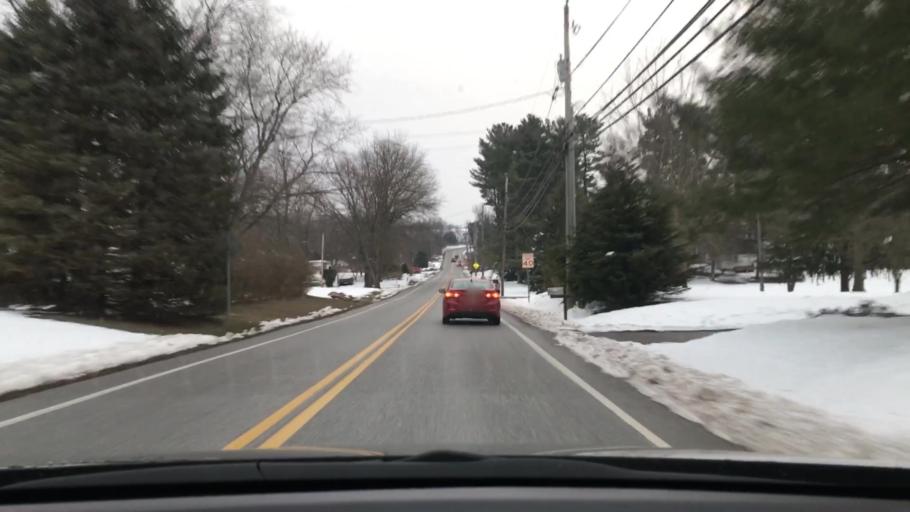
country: US
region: Pennsylvania
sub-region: York County
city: Dover
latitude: 39.9868
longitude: -76.8557
